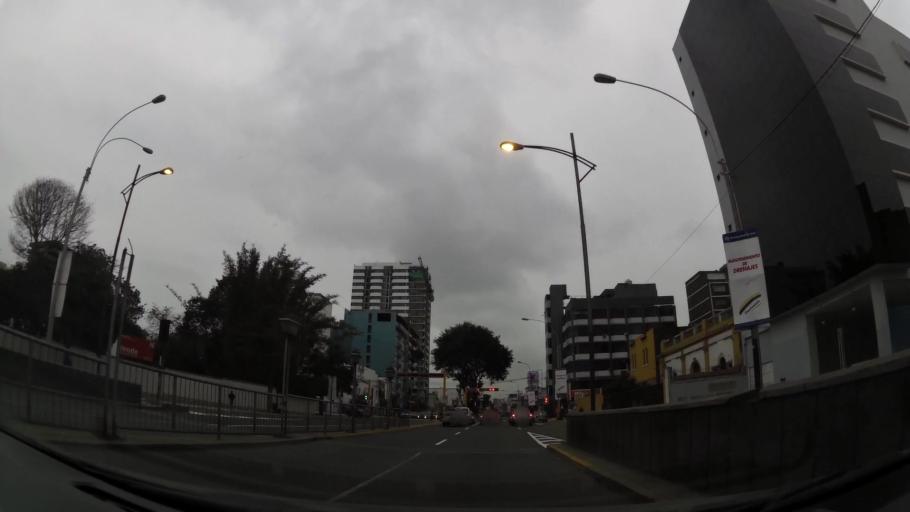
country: PE
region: Lima
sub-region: Lima
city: San Isidro
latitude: -12.0913
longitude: -77.0335
